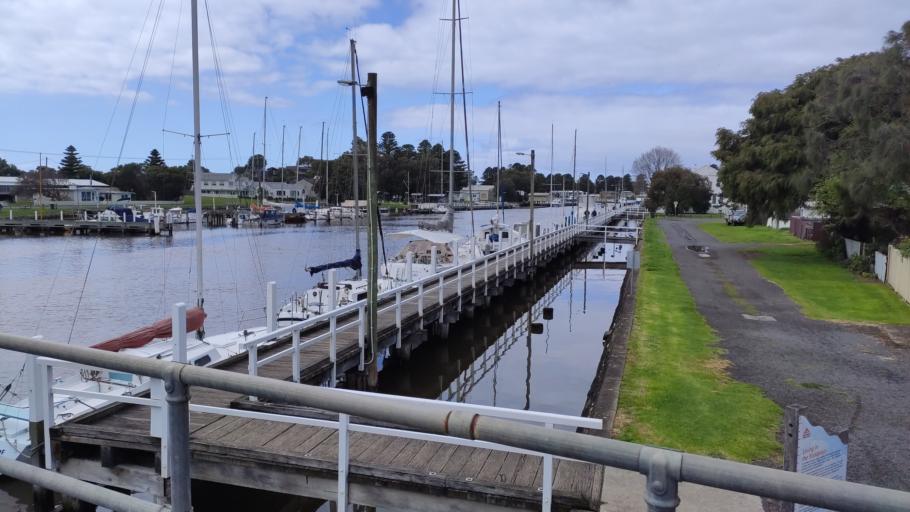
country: AU
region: Victoria
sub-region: Moyne
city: Port Fairy
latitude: -38.3848
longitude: 142.2402
